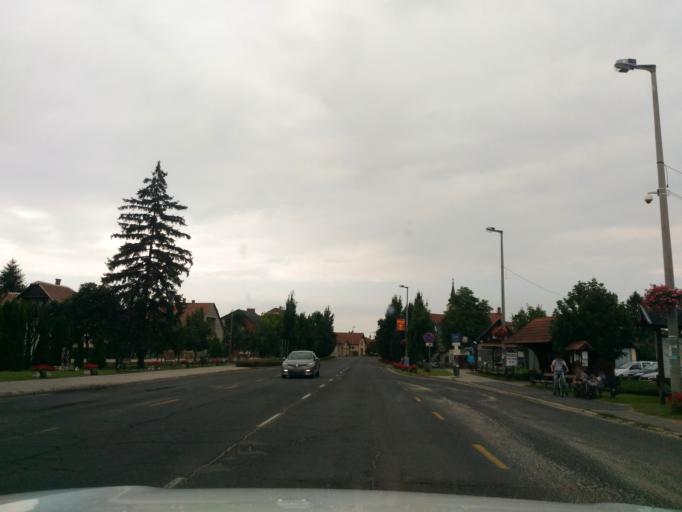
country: HU
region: Pest
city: Alsonemedi
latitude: 47.3112
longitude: 19.1703
